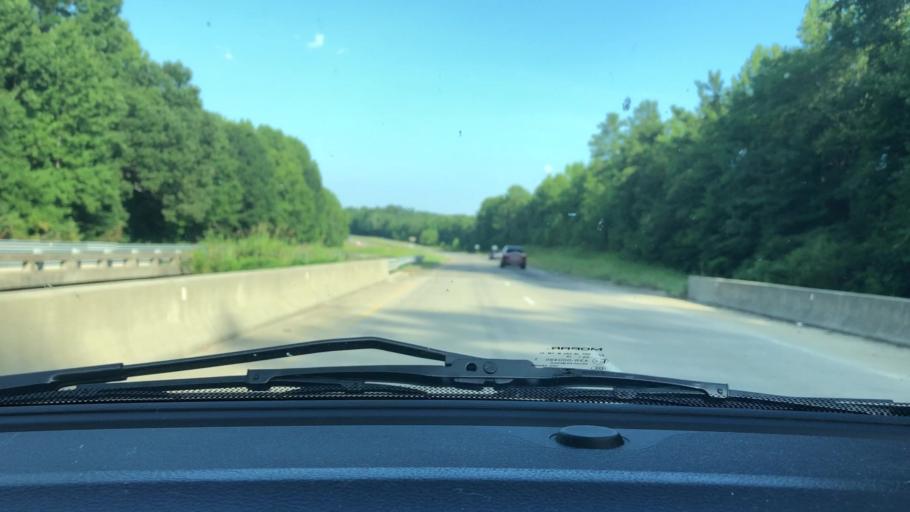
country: US
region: North Carolina
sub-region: Chatham County
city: Farmville
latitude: 35.6124
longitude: -79.3440
